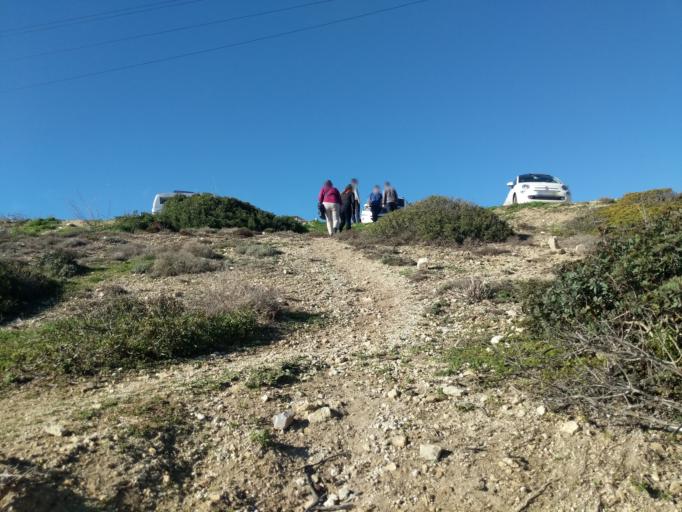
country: PT
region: Faro
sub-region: Vila do Bispo
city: Sagres
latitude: 37.0062
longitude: -8.9386
